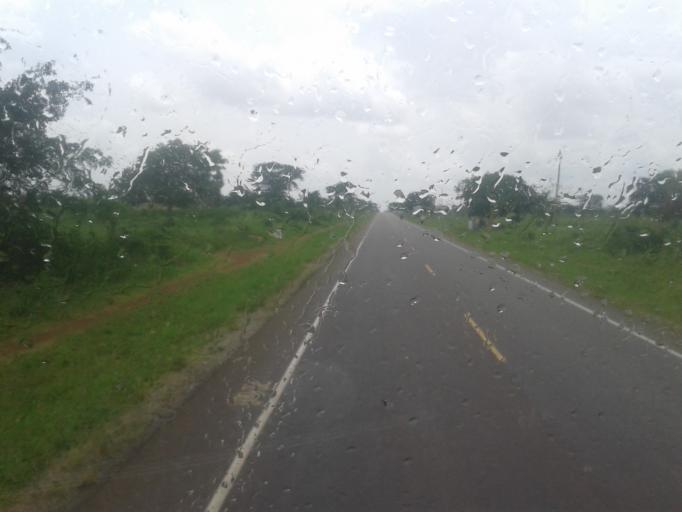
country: UG
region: Western Region
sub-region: Kiryandongo District
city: Masindi Port
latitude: 1.7151
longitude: 32.0277
